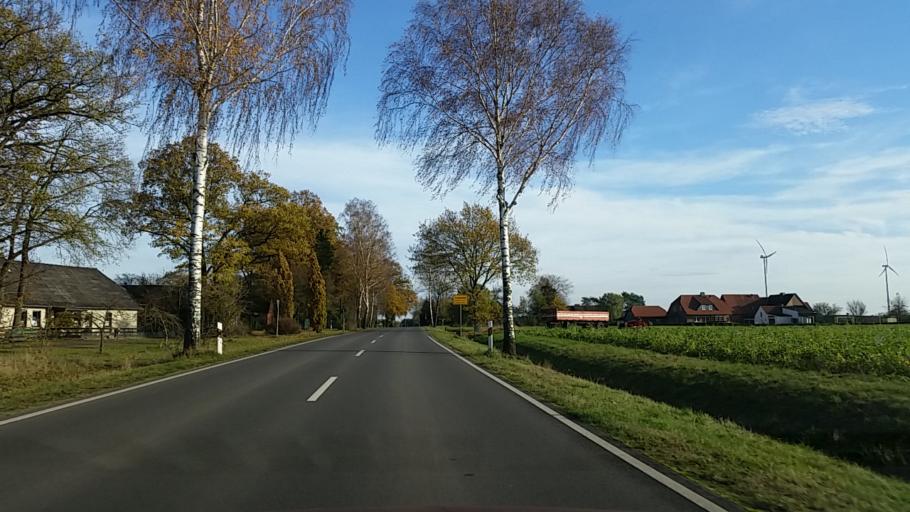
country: DE
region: Lower Saxony
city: Dedelstorf
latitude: 52.6771
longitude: 10.5371
